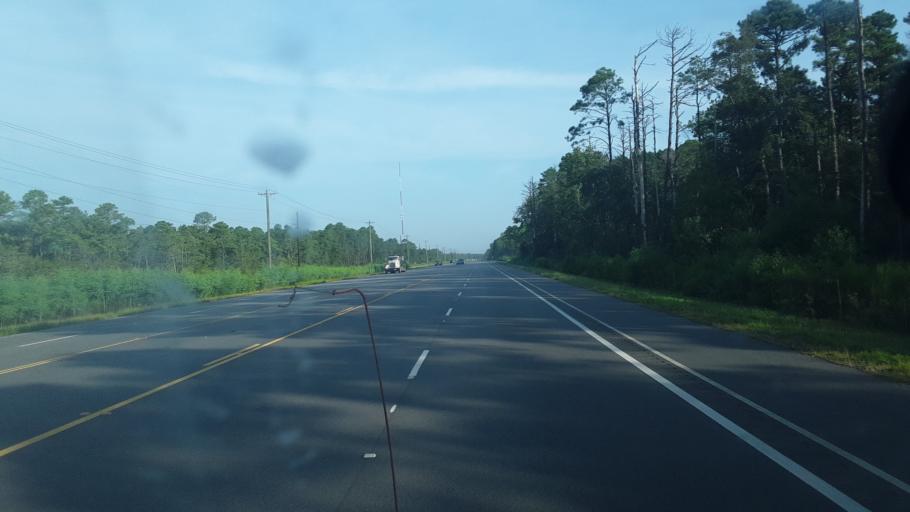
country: US
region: South Carolina
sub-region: Horry County
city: Myrtle Beach
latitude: 33.7742
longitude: -78.8705
